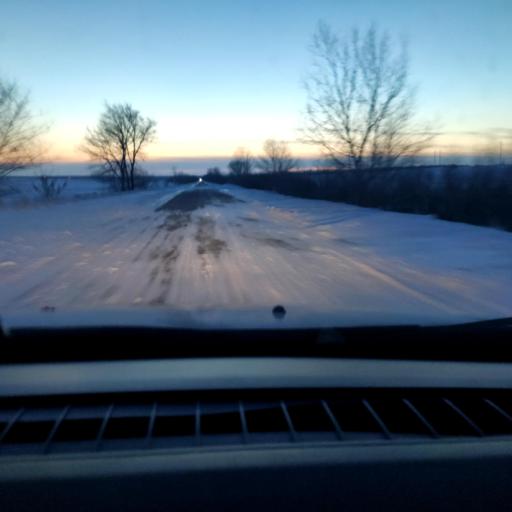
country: RU
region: Samara
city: Georgiyevka
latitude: 53.3389
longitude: 50.9561
